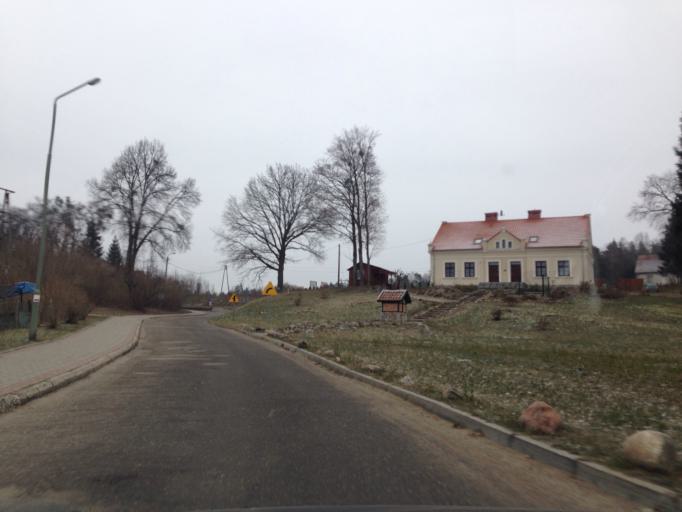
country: PL
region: Warmian-Masurian Voivodeship
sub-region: Powiat ketrzynski
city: Reszel
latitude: 54.0253
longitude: 21.2178
